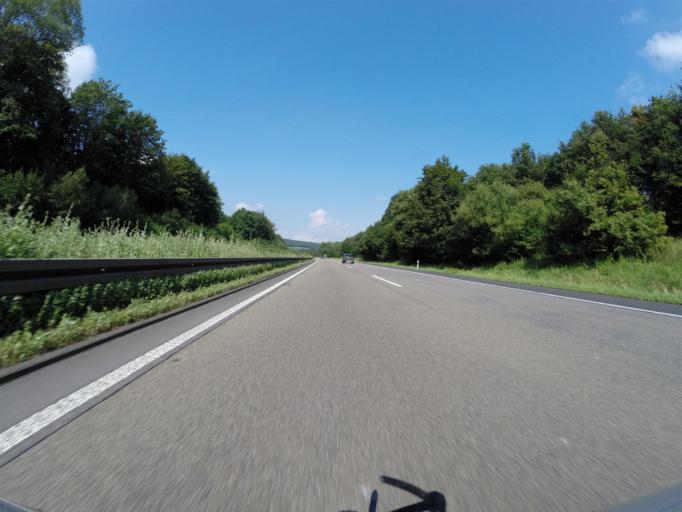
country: DE
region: Hesse
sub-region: Regierungsbezirk Kassel
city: Martinhagen
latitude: 51.3018
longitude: 9.3227
